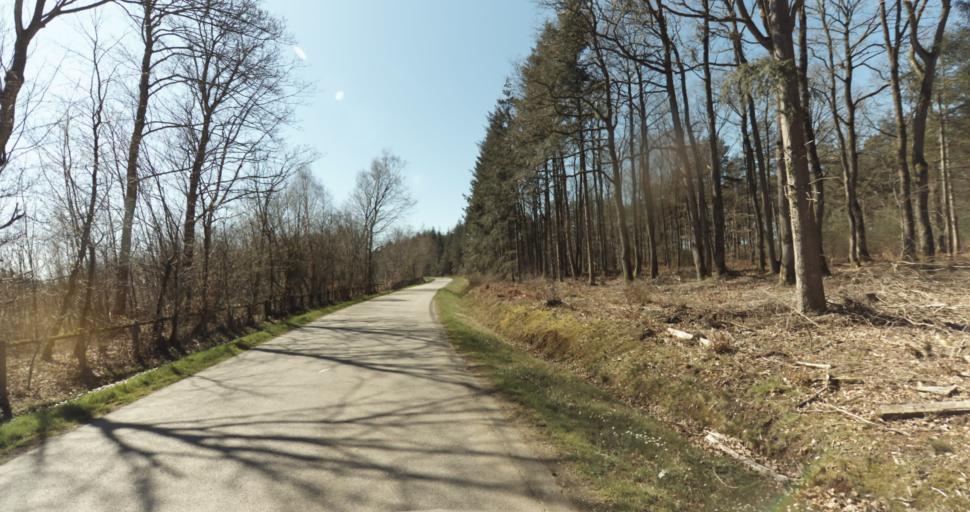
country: FR
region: Lower Normandy
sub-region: Departement du Calvados
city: Livarot
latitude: 48.9701
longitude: 0.1007
